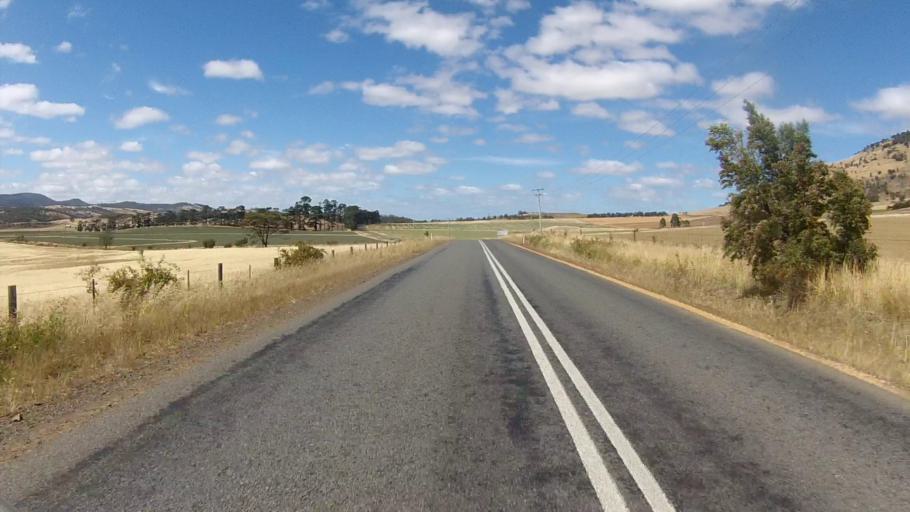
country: AU
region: Tasmania
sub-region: Sorell
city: Sorell
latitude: -42.6323
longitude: 147.4297
